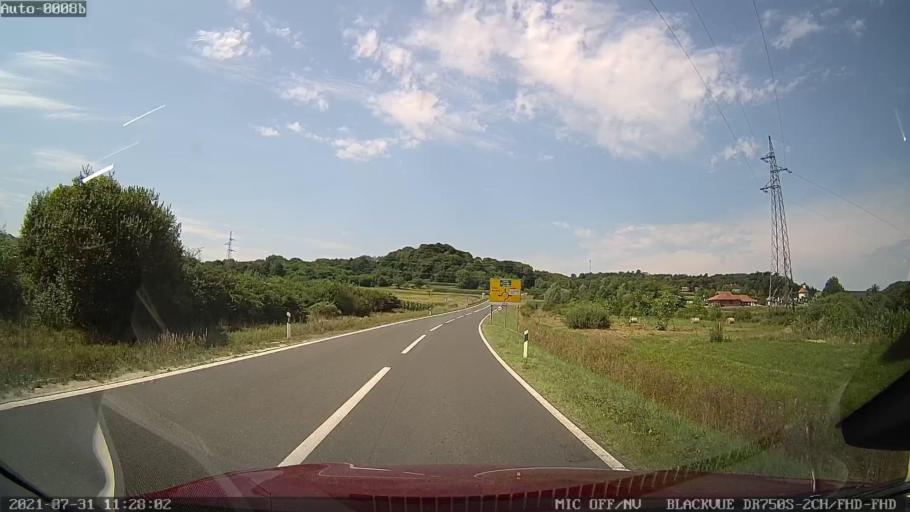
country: HR
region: Varazdinska
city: Ljubescica
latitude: 46.2037
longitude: 16.4280
